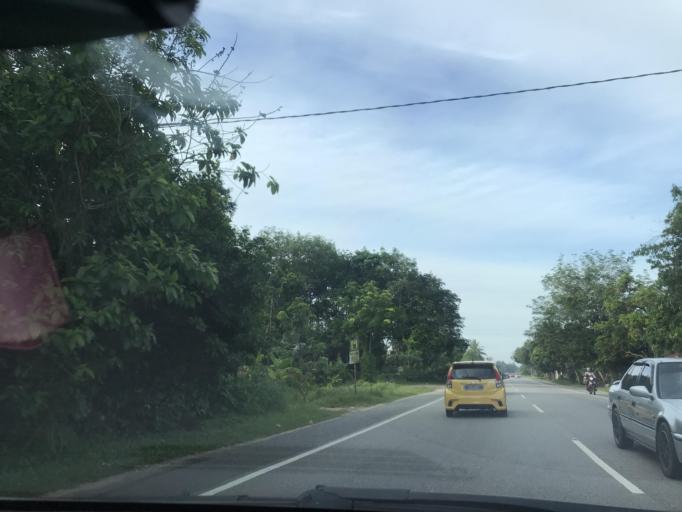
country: MY
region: Kelantan
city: Kampong Pangkal Kalong
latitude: 5.9617
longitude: 102.1937
